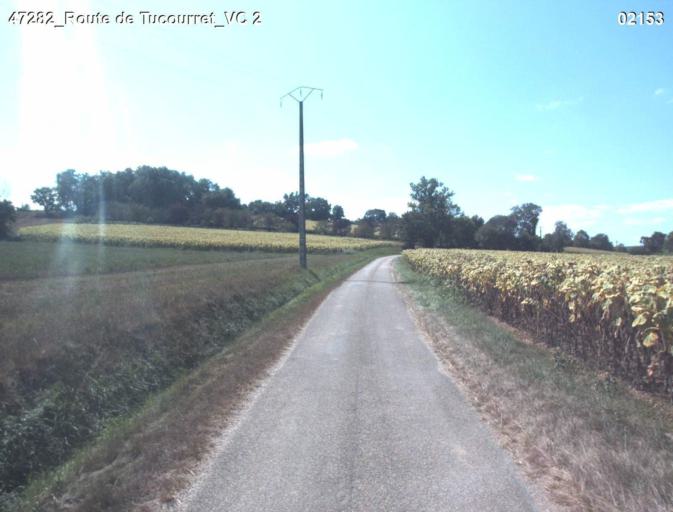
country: FR
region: Aquitaine
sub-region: Departement du Lot-et-Garonne
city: Laplume
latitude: 44.1046
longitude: 0.4927
